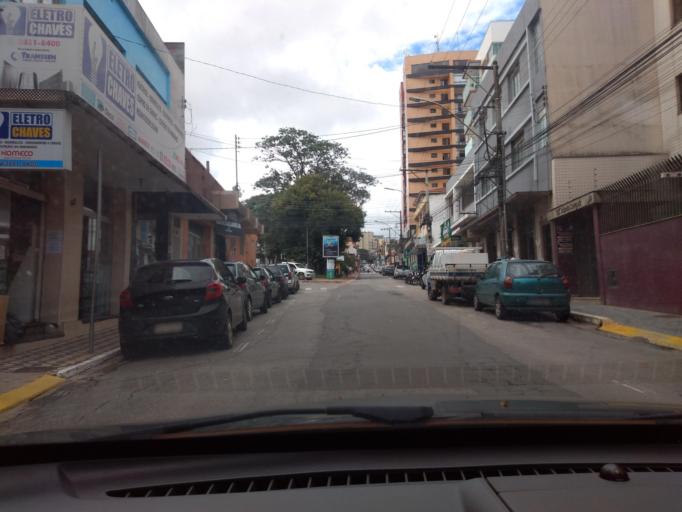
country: BR
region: Minas Gerais
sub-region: Lavras
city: Lavras
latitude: -21.2366
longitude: -44.9980
